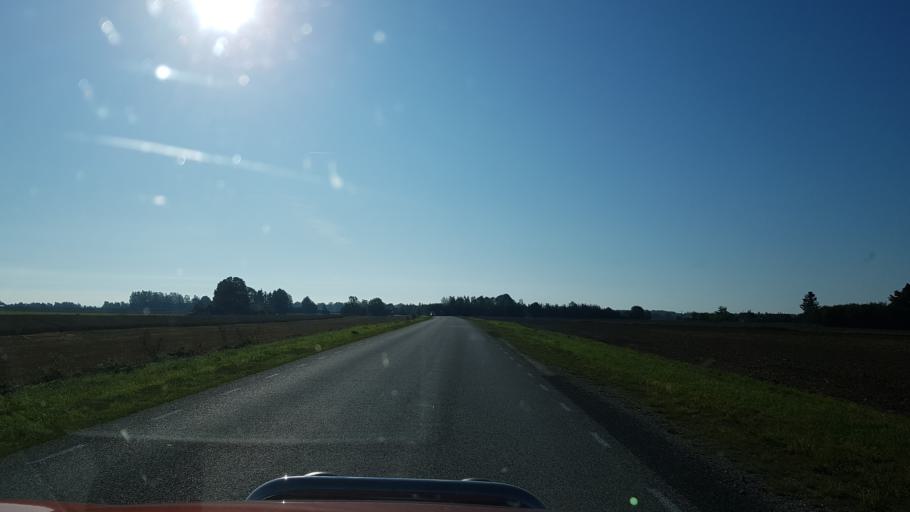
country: EE
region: Jogevamaa
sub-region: Tabivere vald
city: Tabivere
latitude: 58.6781
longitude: 26.6675
